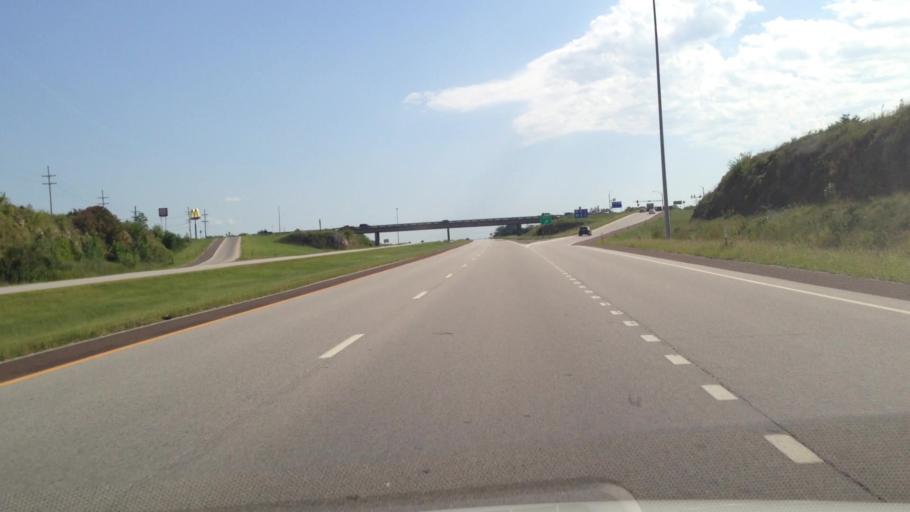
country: US
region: Kansas
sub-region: Miami County
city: Louisburg
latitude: 38.6244
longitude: -94.6952
